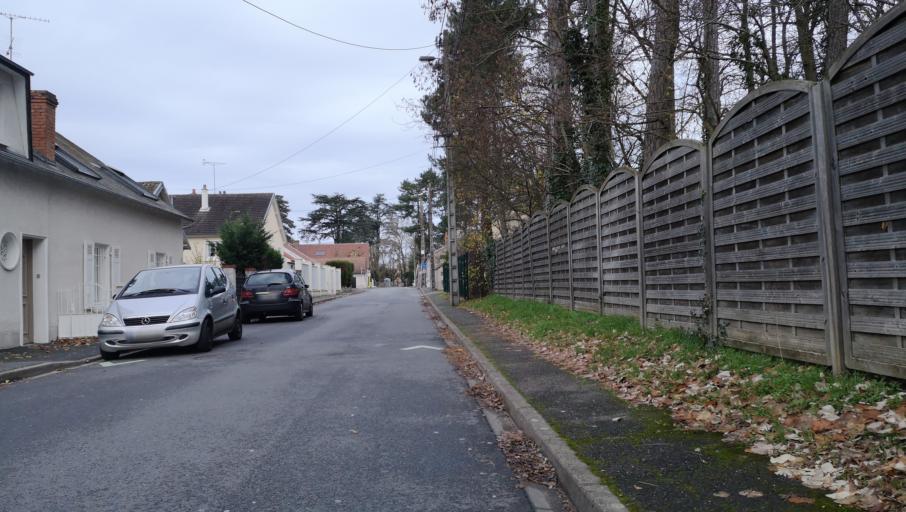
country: FR
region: Centre
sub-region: Departement du Loiret
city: Saint-Jean-de-Braye
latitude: 47.9086
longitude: 1.9834
